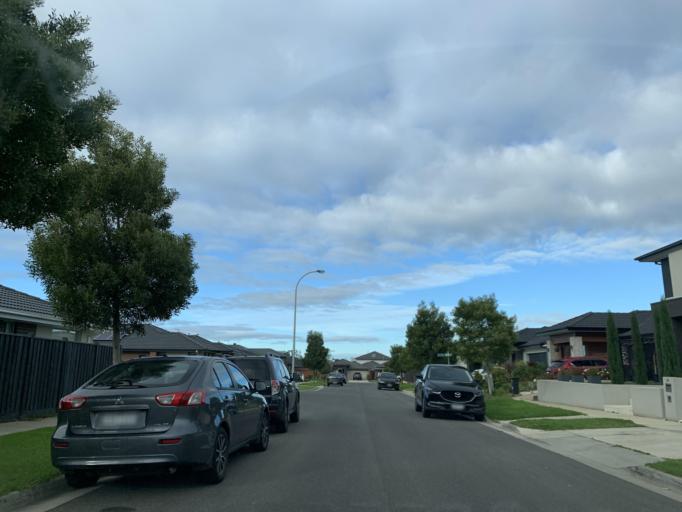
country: AU
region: Victoria
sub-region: Casey
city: Cranbourne East
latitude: -38.1227
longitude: 145.3374
